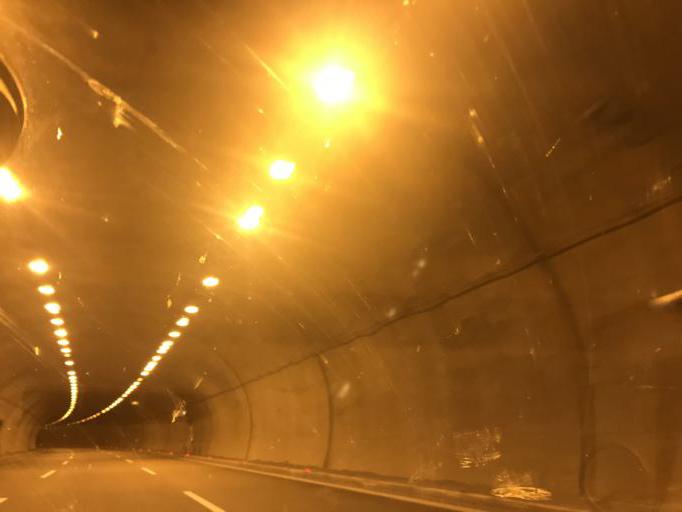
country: TR
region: Nigde
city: Ciftehan
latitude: 37.5498
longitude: 34.7814
